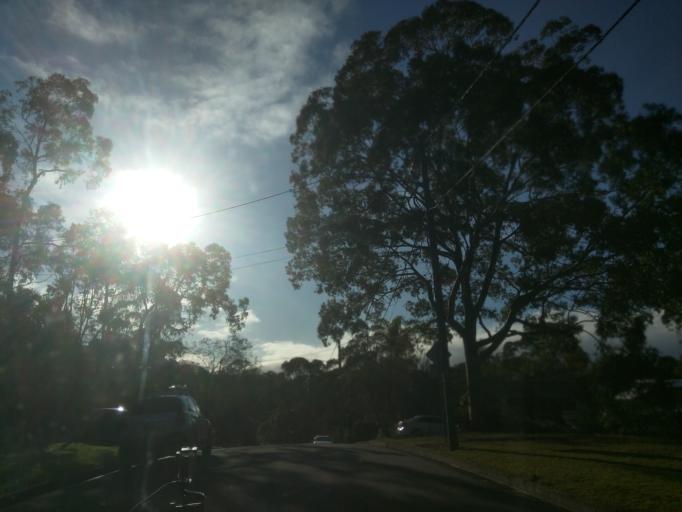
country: AU
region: New South Wales
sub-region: Hurstville
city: Lugarno
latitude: -33.9886
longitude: 151.0425
